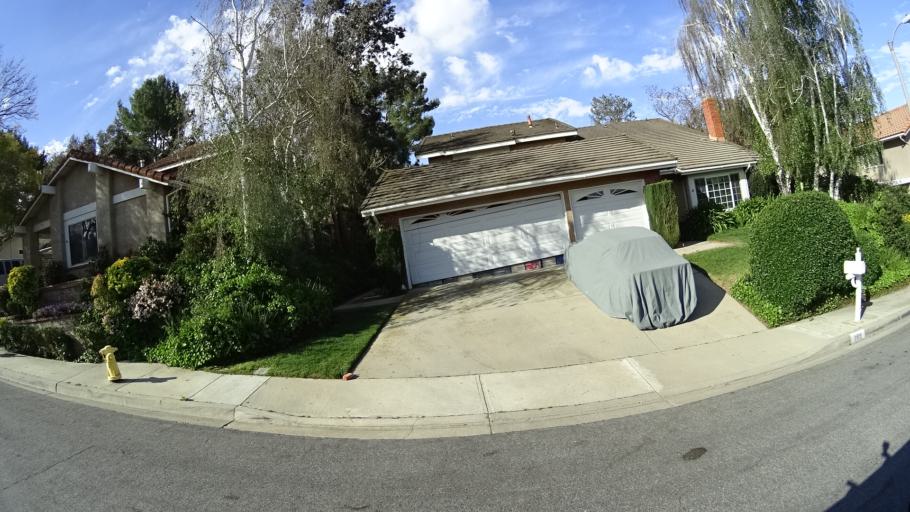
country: US
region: California
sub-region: Ventura County
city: Casa Conejo
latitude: 34.1715
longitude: -118.9478
